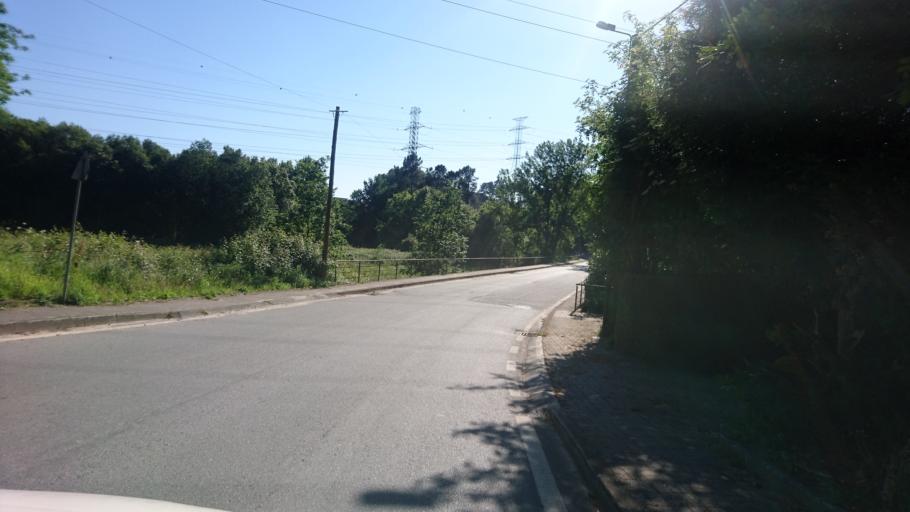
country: PT
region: Porto
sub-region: Paredes
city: Casteloes de Cepeda
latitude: 41.1896
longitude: -8.3354
